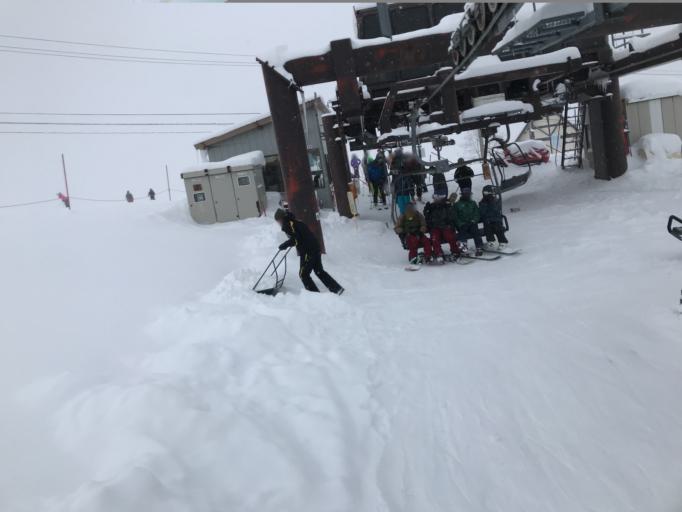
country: JP
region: Nagano
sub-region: Kitaazumi Gun
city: Hakuba
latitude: 36.7010
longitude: 137.8104
